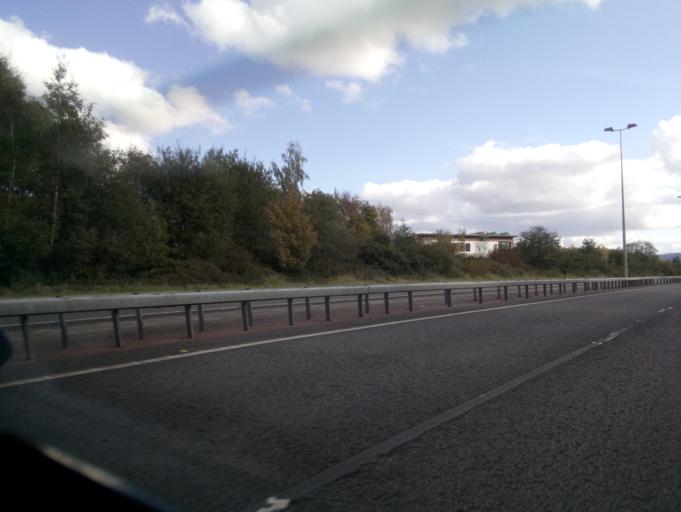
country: GB
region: Wales
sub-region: Merthyr Tydfil County Borough
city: Merthyr Tydfil
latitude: 51.7465
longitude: -3.3919
